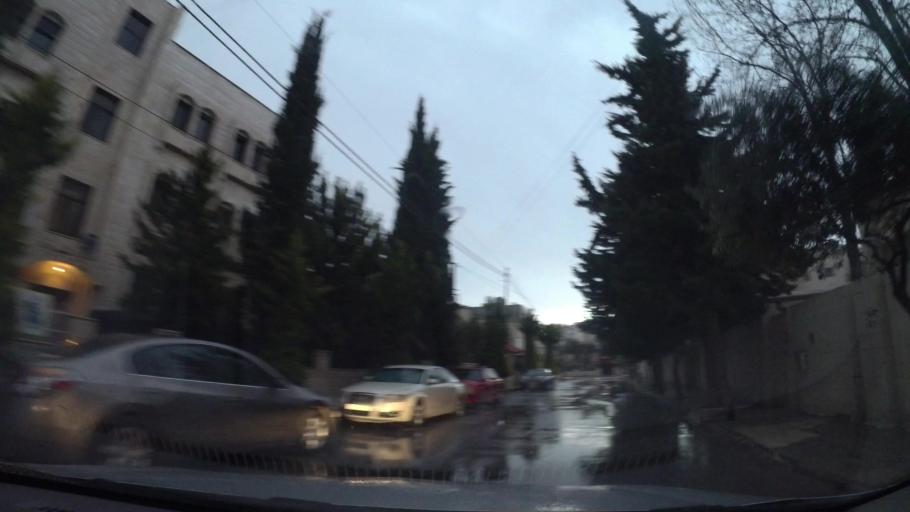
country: JO
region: Amman
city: Umm as Summaq
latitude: 31.9023
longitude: 35.8577
